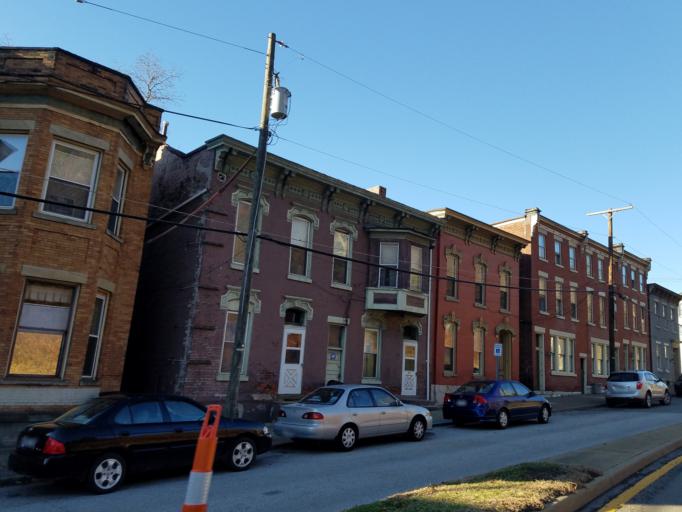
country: US
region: West Virginia
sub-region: Ohio County
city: Wheeling
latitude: 40.0730
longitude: -80.7230
